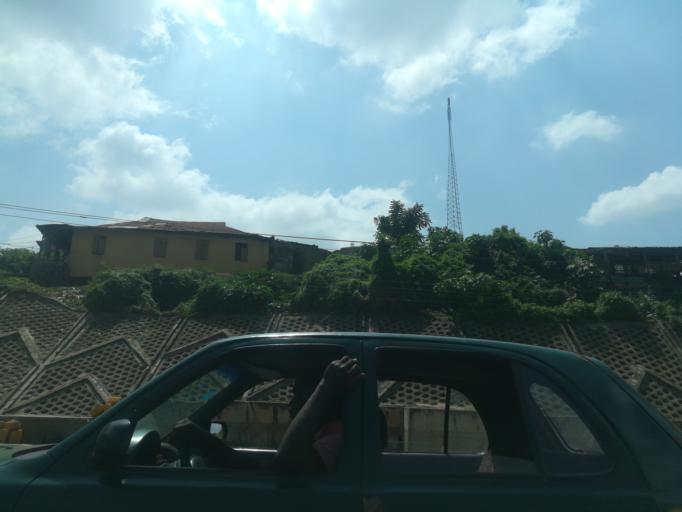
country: NG
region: Ogun
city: Abeokuta
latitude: 7.1567
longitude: 3.3352
